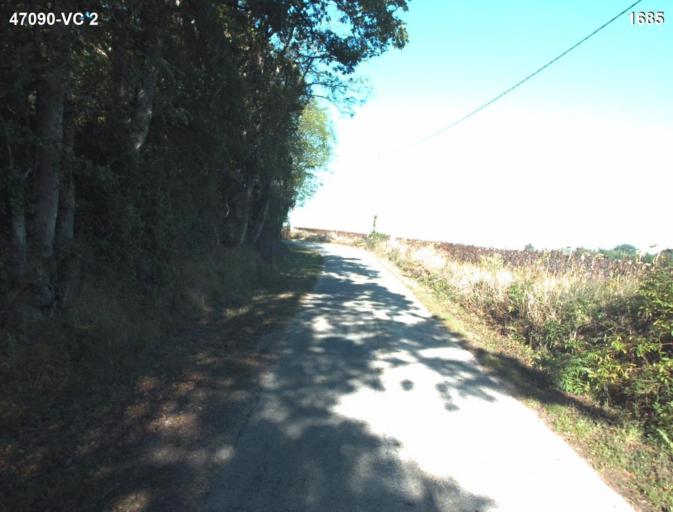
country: FR
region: Aquitaine
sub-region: Departement du Lot-et-Garonne
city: Nerac
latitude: 44.1789
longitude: 0.3730
